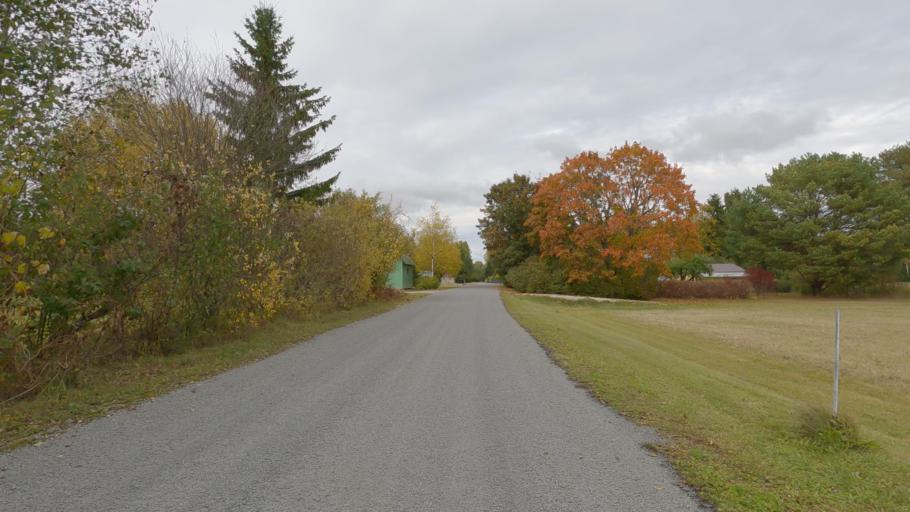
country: EE
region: Raplamaa
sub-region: Rapla vald
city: Rapla
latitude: 58.9873
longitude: 24.7803
